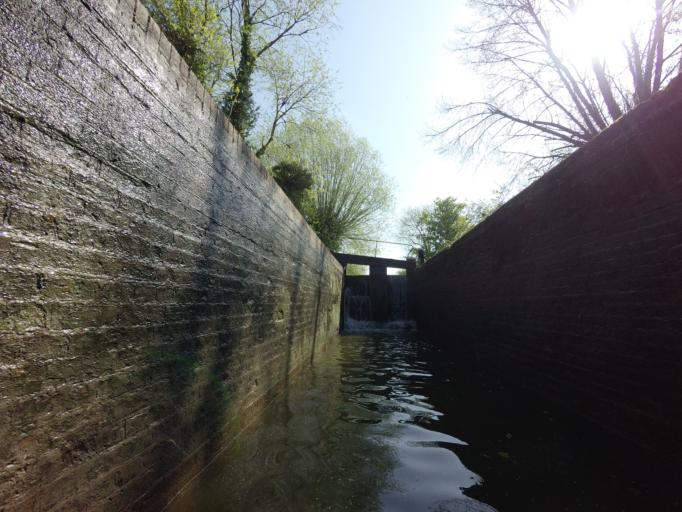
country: GB
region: England
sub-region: Buckinghamshire
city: Cheddington
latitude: 51.8210
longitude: -0.6884
